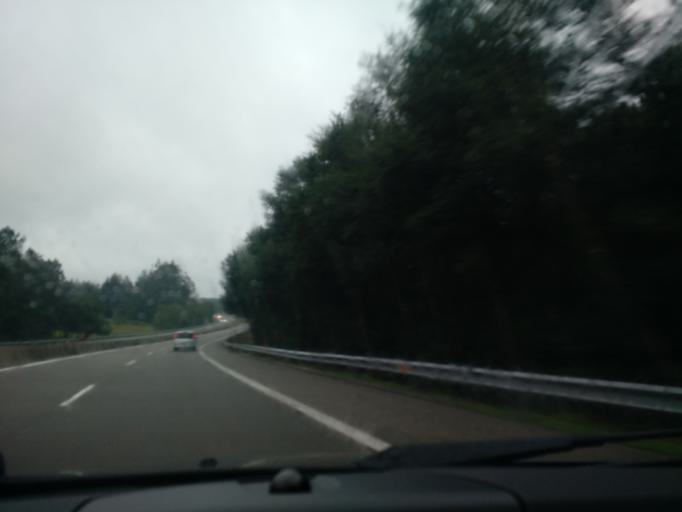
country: ES
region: Galicia
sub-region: Provincia da Coruna
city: Ordes
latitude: 43.0566
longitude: -8.3712
